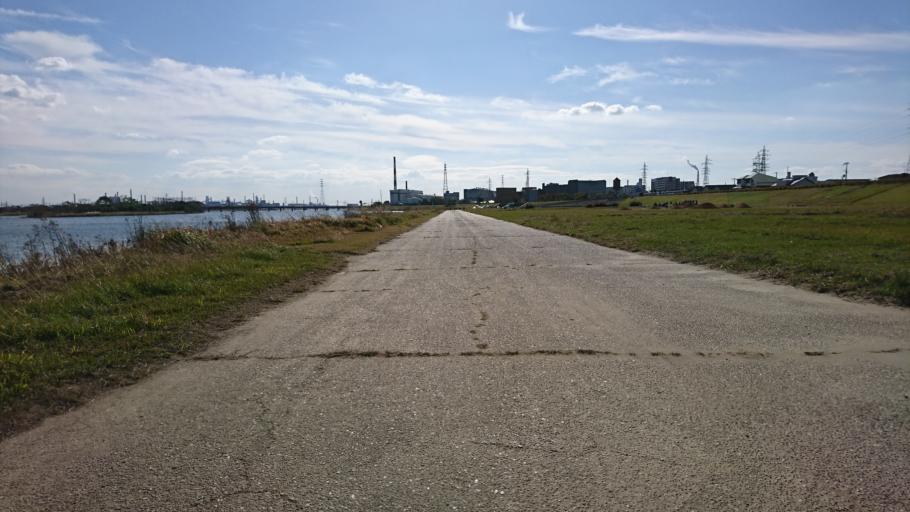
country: JP
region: Hyogo
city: Kakogawacho-honmachi
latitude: 34.7593
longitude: 134.8058
